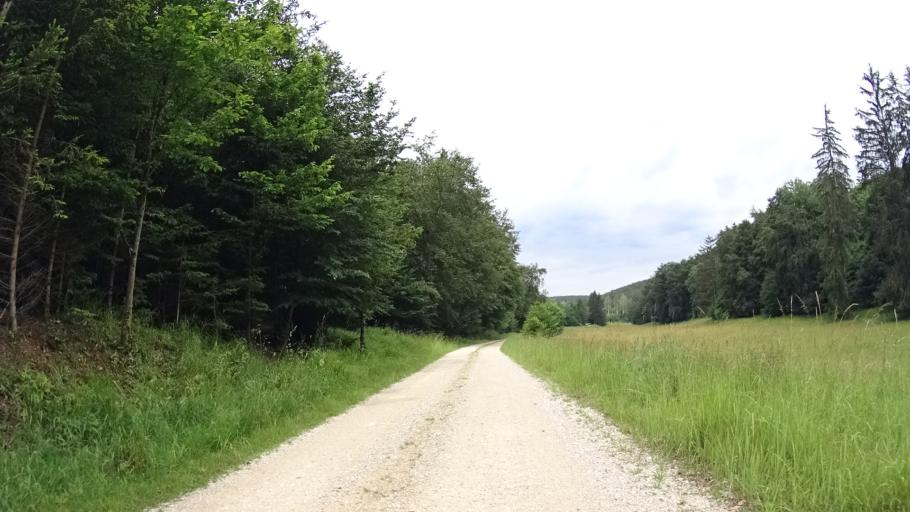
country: DE
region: Bavaria
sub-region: Upper Bavaria
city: Denkendorf
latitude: 48.9157
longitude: 11.5348
